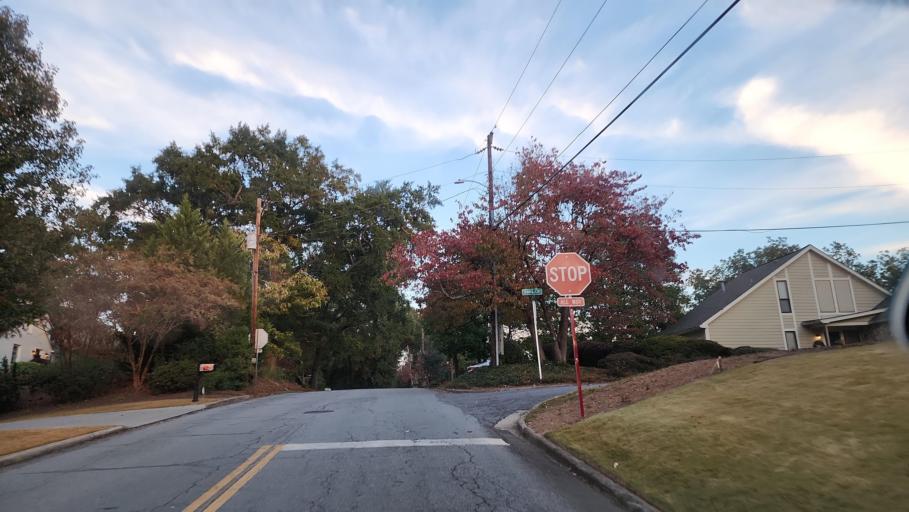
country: US
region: Georgia
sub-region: Fulton County
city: Roswell
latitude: 34.0307
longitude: -84.3647
